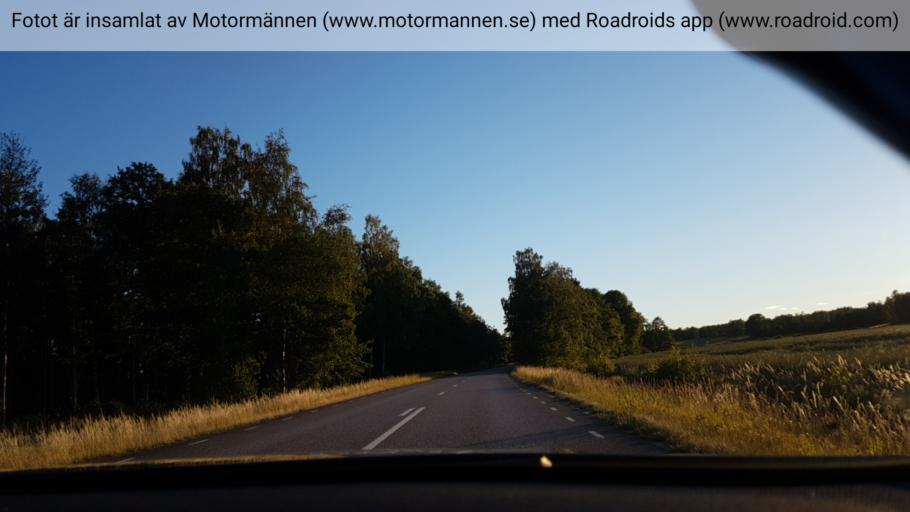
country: SE
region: Vaestra Goetaland
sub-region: Hjo Kommun
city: Hjo
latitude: 58.3216
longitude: 14.3016
